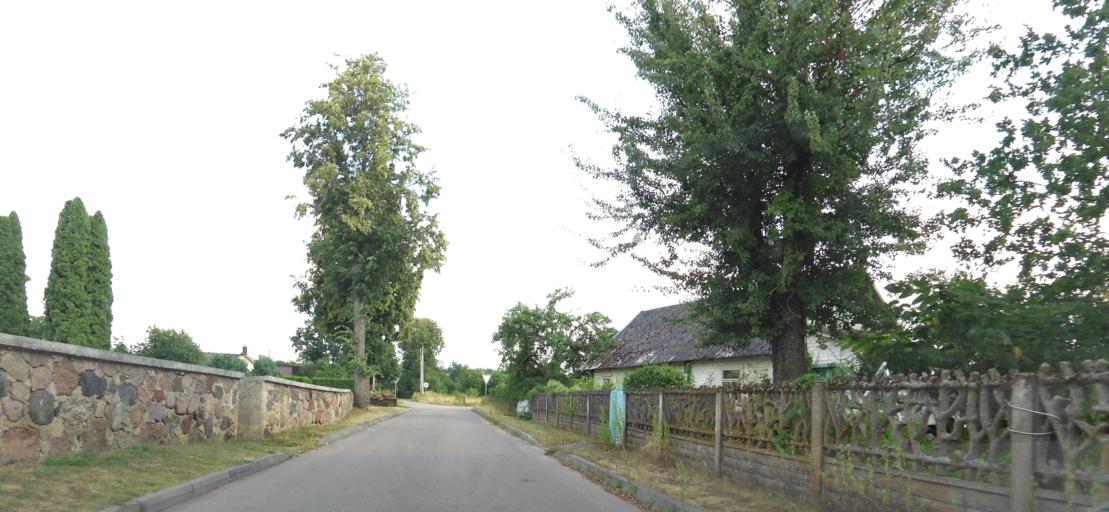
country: LT
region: Alytaus apskritis
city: Varena
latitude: 54.2139
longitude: 24.4179
